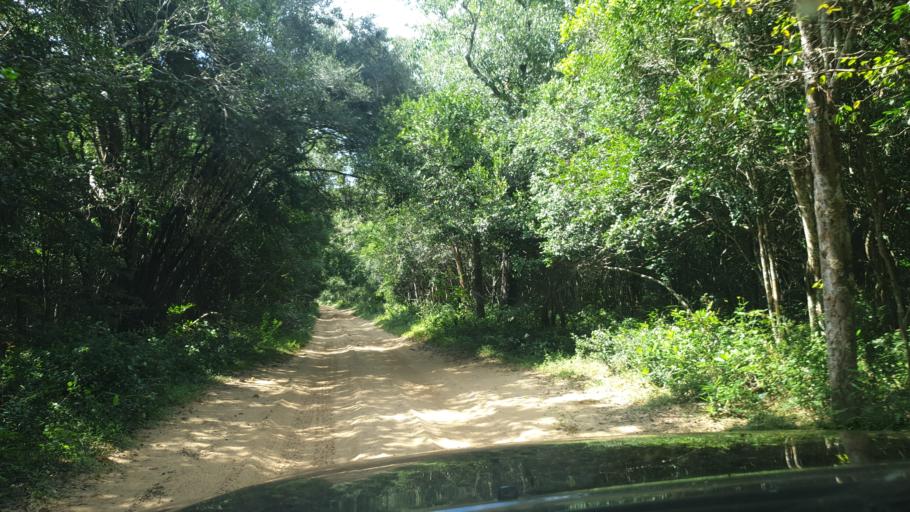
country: LK
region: North Central
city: Anuradhapura
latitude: 8.4173
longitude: 80.0233
